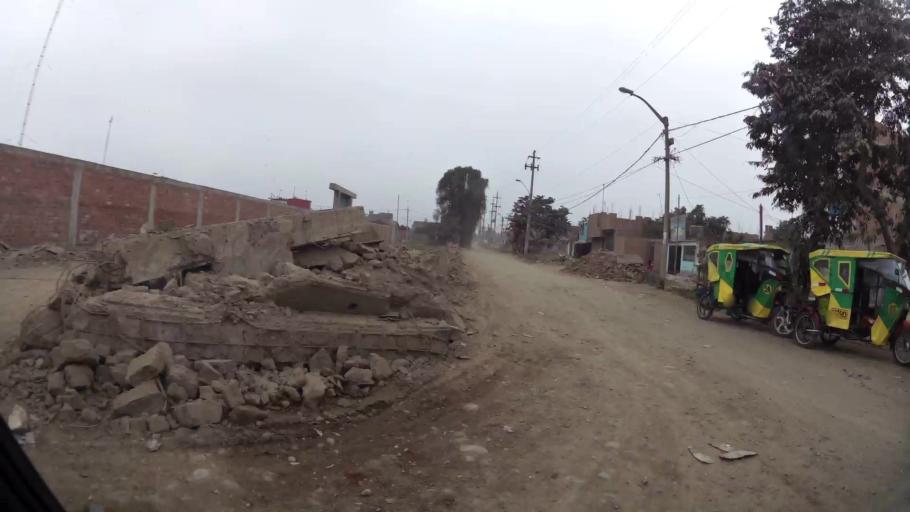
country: PE
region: Lima
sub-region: Lima
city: Urb. Santo Domingo
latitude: -11.8895
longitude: -77.0595
